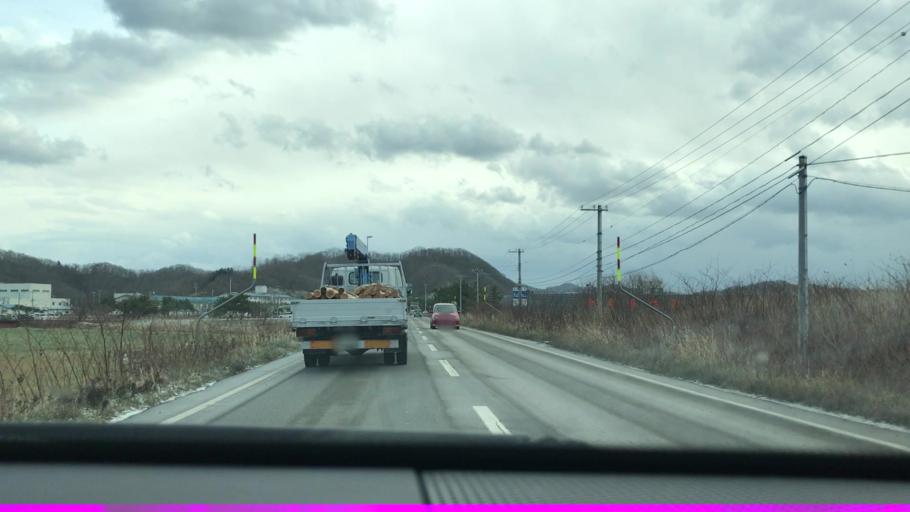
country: JP
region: Hokkaido
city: Shizunai-furukawacho
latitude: 42.3090
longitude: 142.4339
